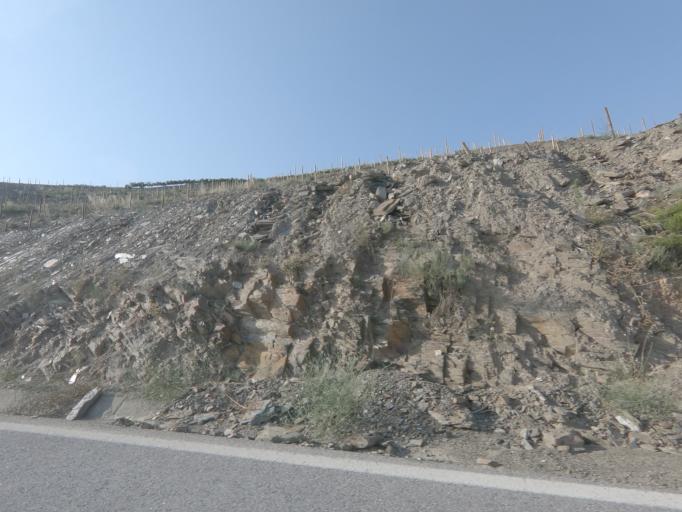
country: PT
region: Viseu
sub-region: Tabuaco
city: Tabuaco
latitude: 41.1399
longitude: -7.5432
